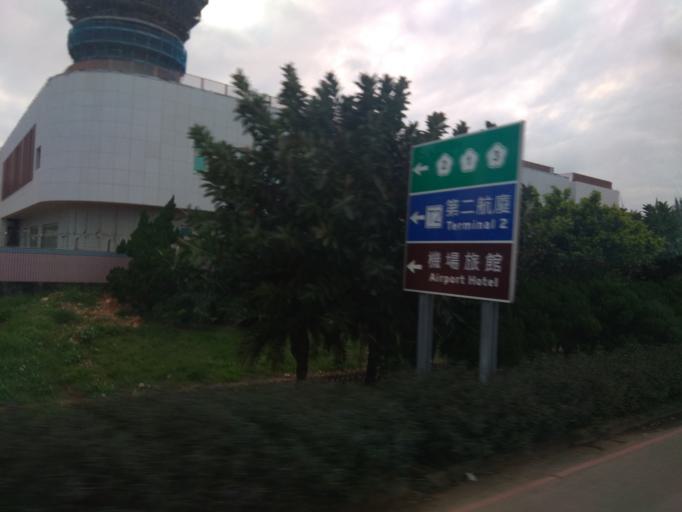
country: TW
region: Taiwan
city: Taoyuan City
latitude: 25.0796
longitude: 121.2348
